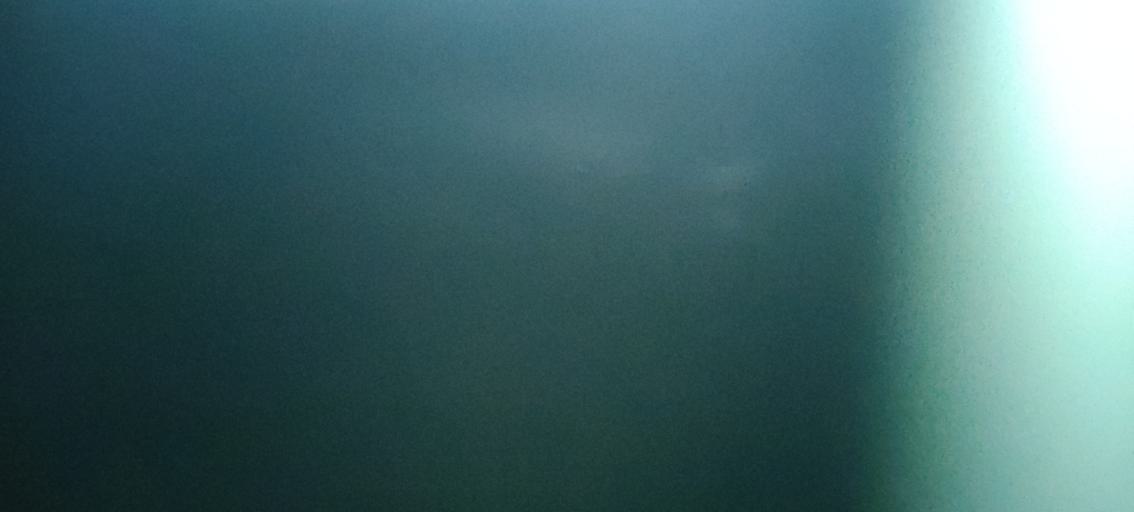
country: IN
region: Kerala
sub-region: Malappuram
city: Ponnani
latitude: 10.7737
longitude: 76.0315
